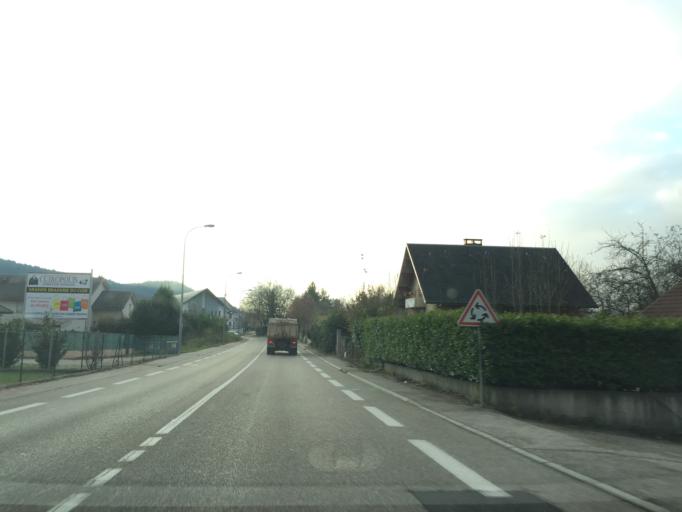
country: FR
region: Rhone-Alpes
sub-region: Departement de la Savoie
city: Sonnaz
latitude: 45.6031
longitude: 5.9133
